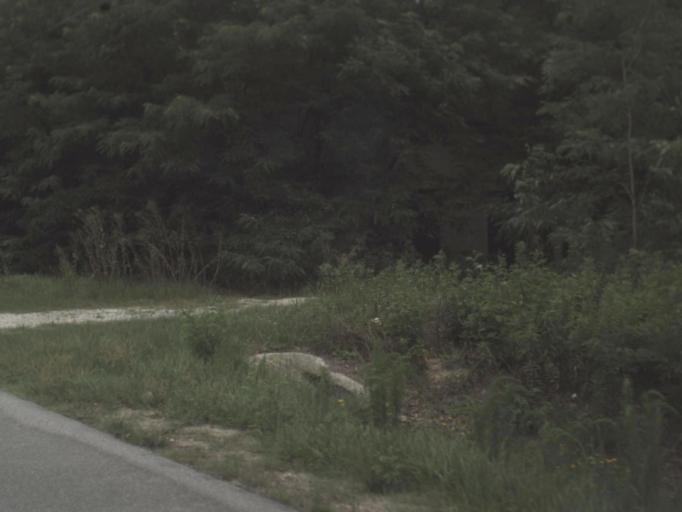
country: US
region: Florida
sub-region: Madison County
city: Madison
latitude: 30.4874
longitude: -83.4186
